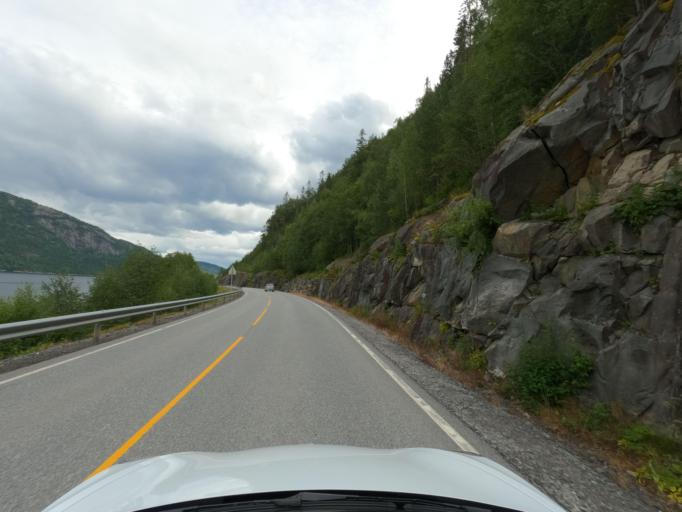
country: NO
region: Telemark
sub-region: Hjartdal
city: Sauland
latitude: 59.8997
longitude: 8.8936
